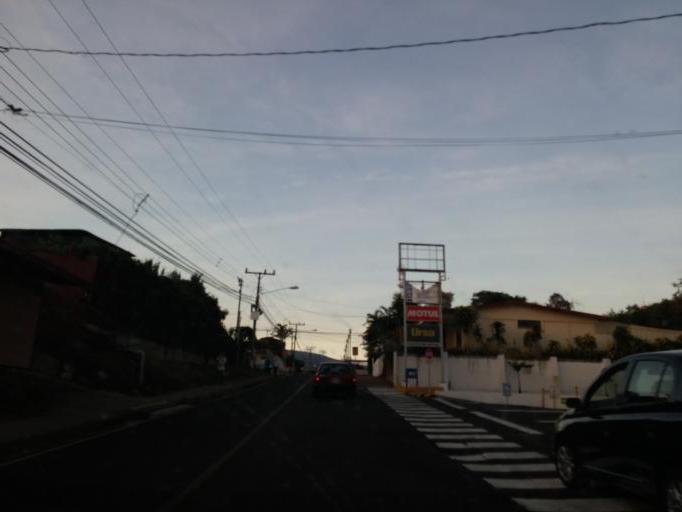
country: CR
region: Alajuela
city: Sabanilla
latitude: 10.0732
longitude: -84.2158
